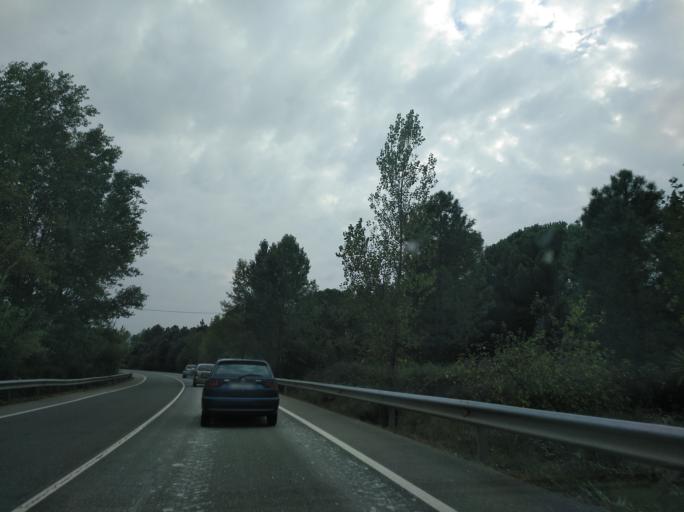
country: ES
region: Catalonia
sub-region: Provincia de Girona
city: Santa Coloma de Farners
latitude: 41.8782
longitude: 2.6580
